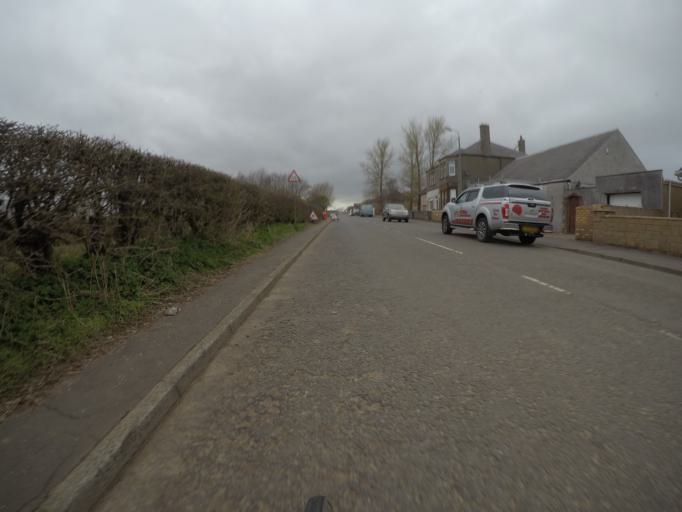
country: GB
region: Scotland
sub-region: North Ayrshire
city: Springside
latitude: 55.6175
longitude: -4.5903
